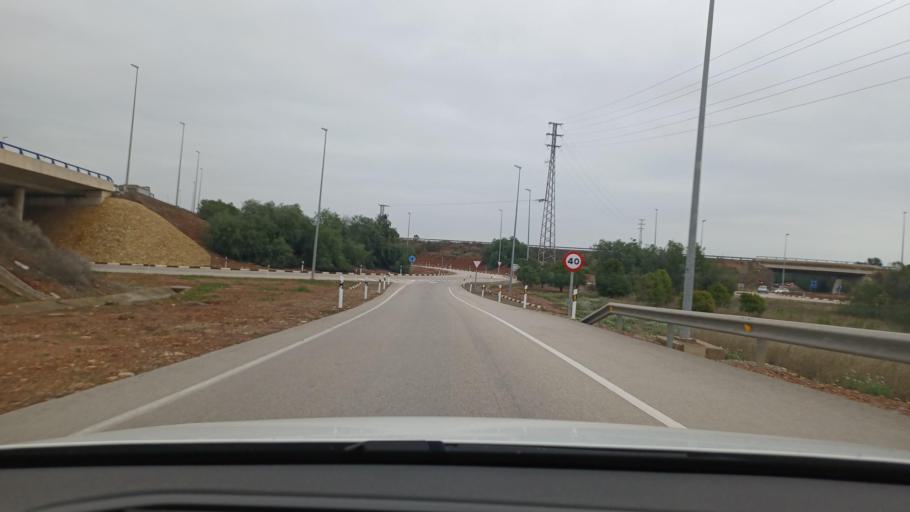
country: ES
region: Valencia
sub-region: Provincia de Castello
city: Villavieja
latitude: 39.8434
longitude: -0.1778
